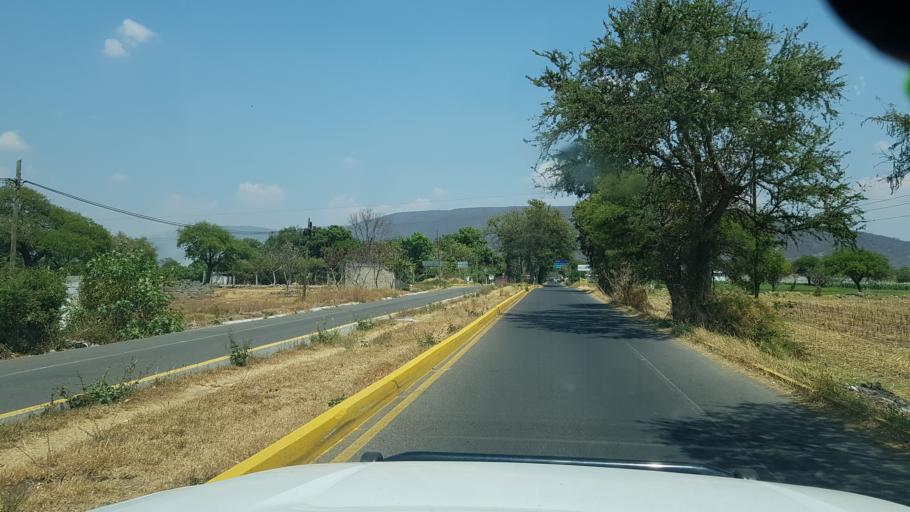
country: MX
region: Puebla
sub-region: Huaquechula
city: Cacaloxuchitl
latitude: 18.7904
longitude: -98.4576
